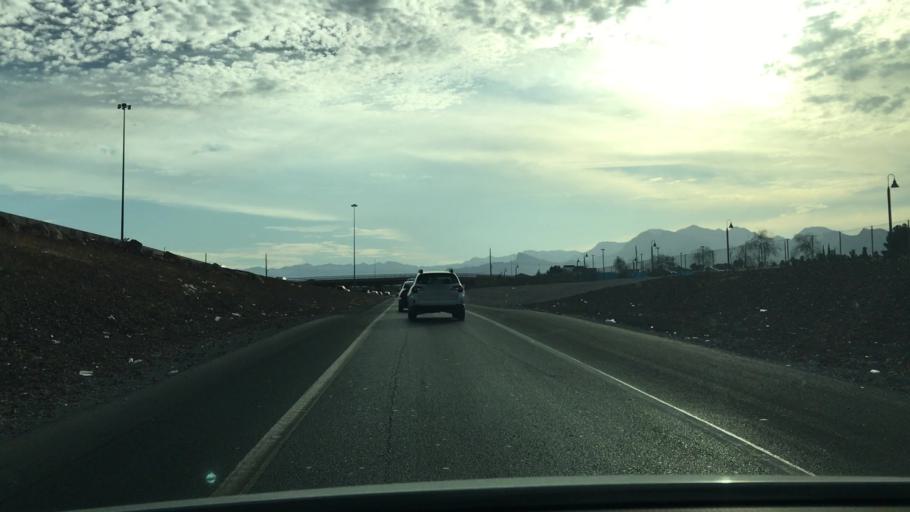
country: US
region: Nevada
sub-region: Clark County
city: Spring Valley
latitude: 36.1786
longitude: -115.2463
